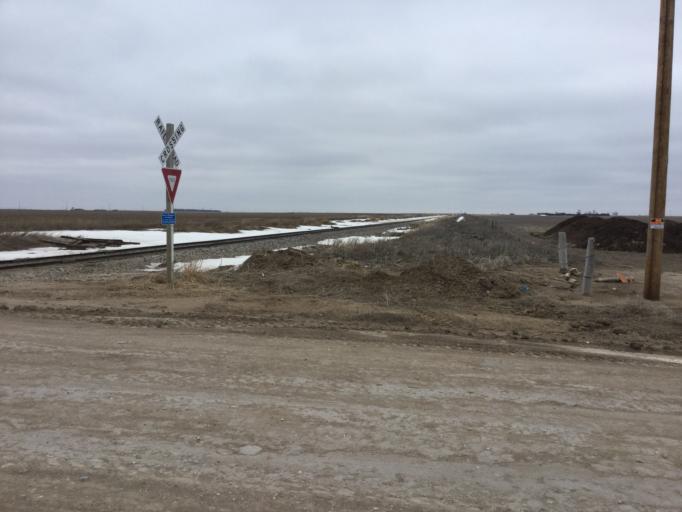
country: US
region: Kansas
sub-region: Scott County
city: Scott City
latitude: 38.4862
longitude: -100.7961
